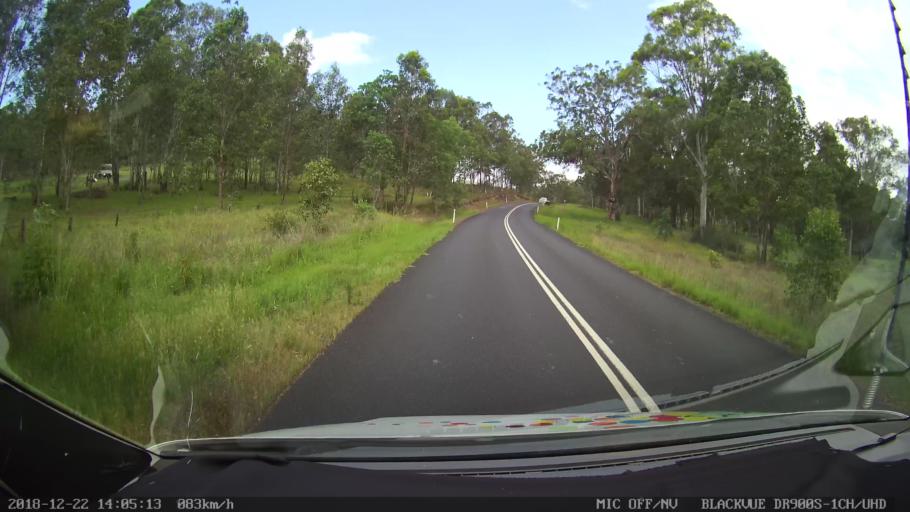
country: AU
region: New South Wales
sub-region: Clarence Valley
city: Coutts Crossing
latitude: -29.9422
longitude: 152.7286
